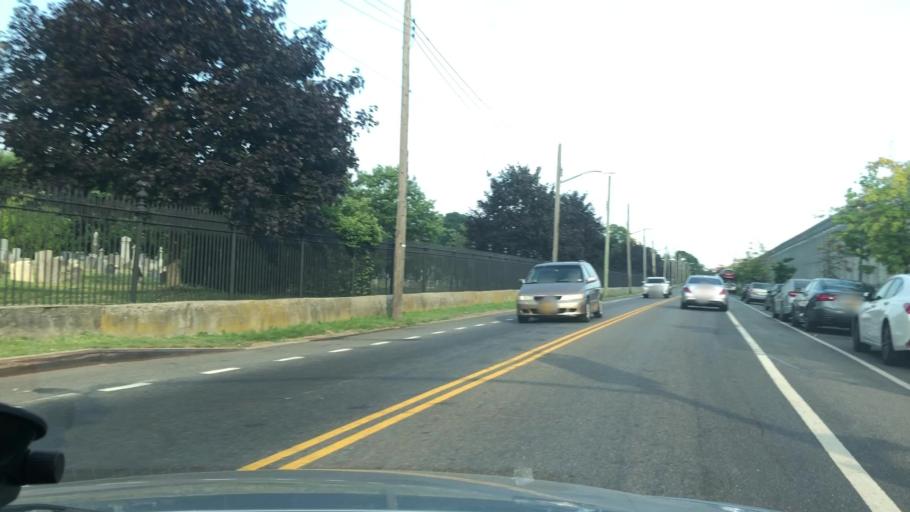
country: US
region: New York
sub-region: Kings County
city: Brooklyn
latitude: 40.6470
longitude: -73.9939
